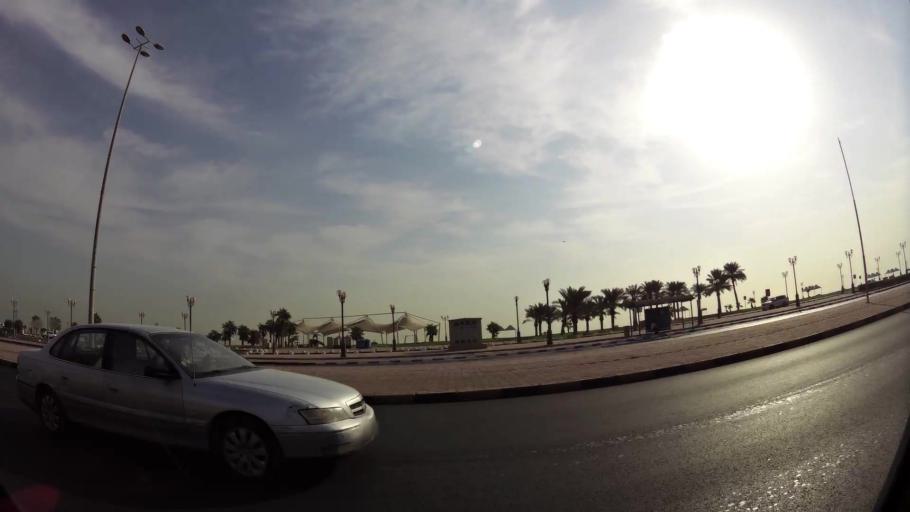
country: KW
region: Muhafazat Hawalli
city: Salwa
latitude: 29.2761
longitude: 48.0885
